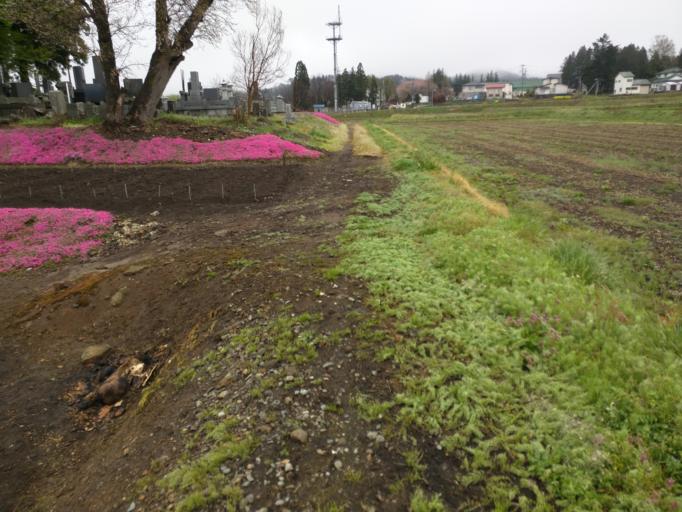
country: JP
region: Fukushima
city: Kitakata
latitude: 37.5414
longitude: 139.9630
